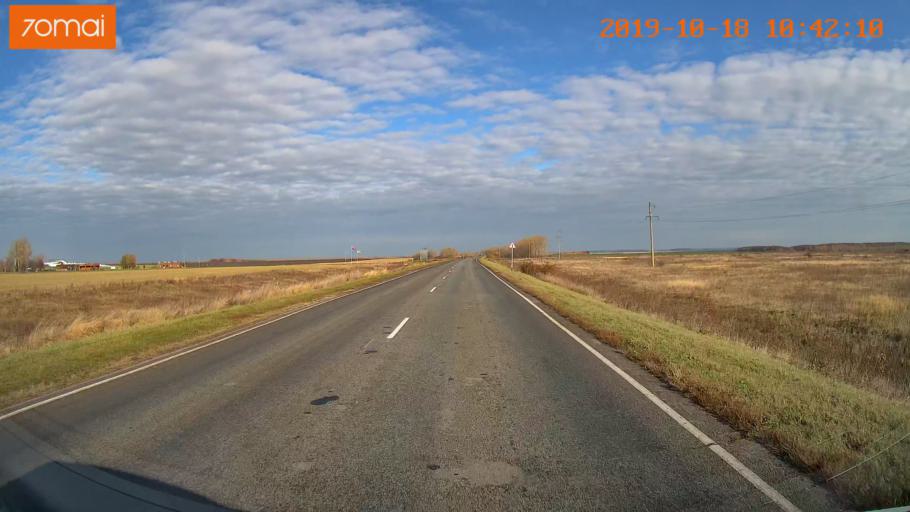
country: RU
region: Tula
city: Kurkino
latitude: 53.6193
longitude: 38.6780
